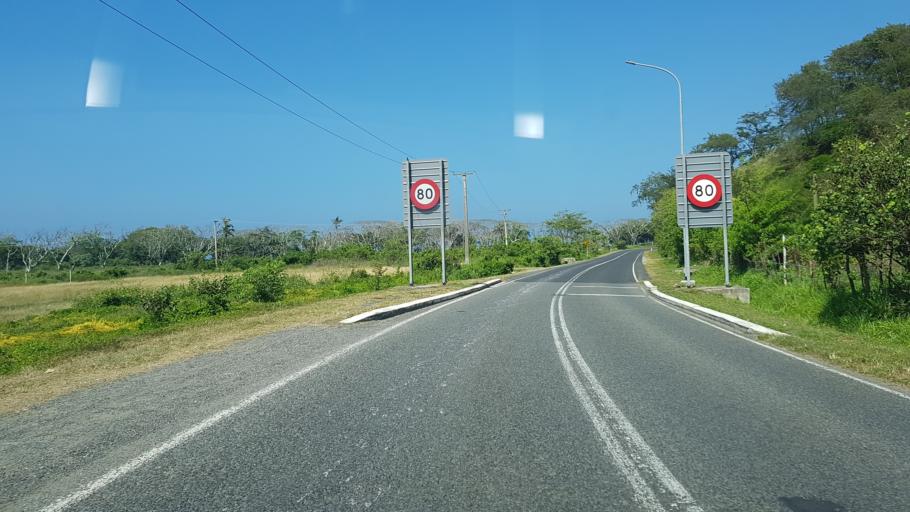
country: FJ
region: Western
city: Nadi
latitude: -18.1838
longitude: 177.6025
